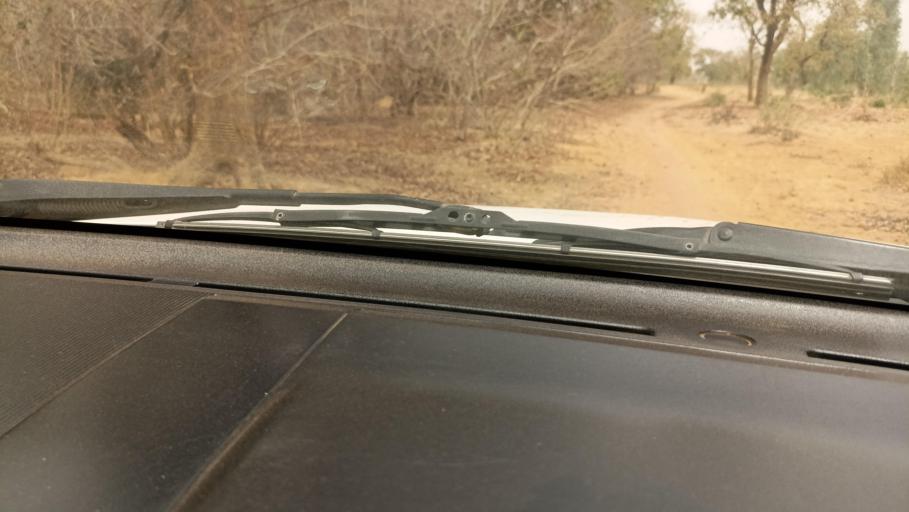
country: BF
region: Boucle du Mouhoun
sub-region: Province du Nayala
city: Toma
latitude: 12.8554
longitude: -2.8021
